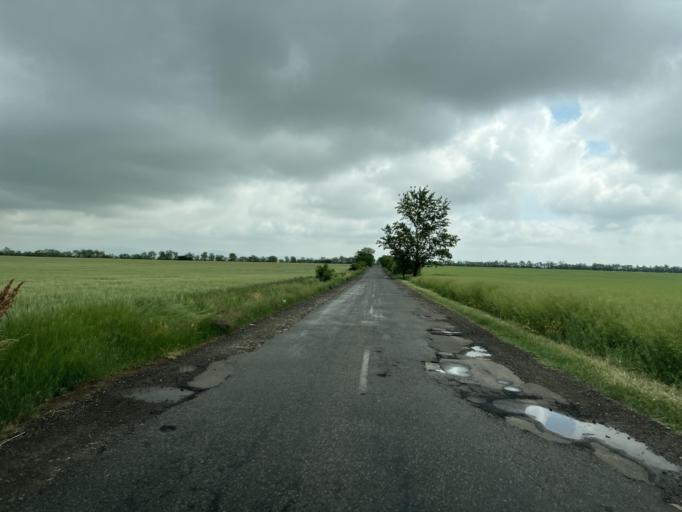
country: HU
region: Nograd
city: Hehalom
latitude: 47.7292
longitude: 19.5726
